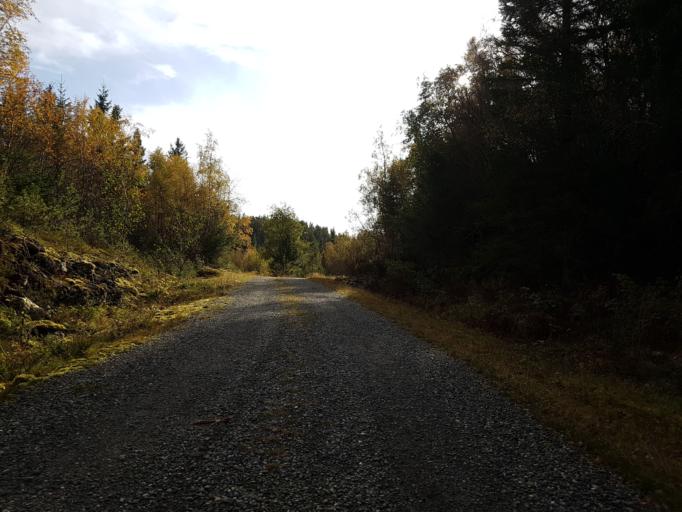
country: NO
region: Sor-Trondelag
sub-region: Trondheim
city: Trondheim
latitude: 63.4491
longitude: 10.2837
